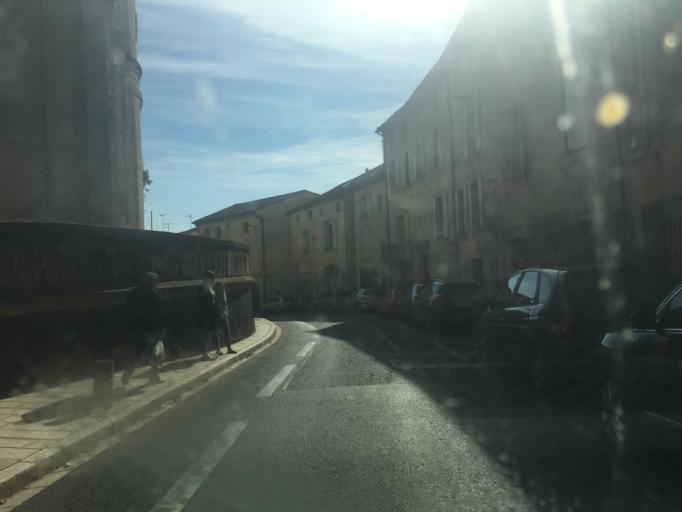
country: FR
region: Languedoc-Roussillon
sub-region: Departement du Gard
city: Uzes
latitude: 44.0109
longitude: 4.4185
